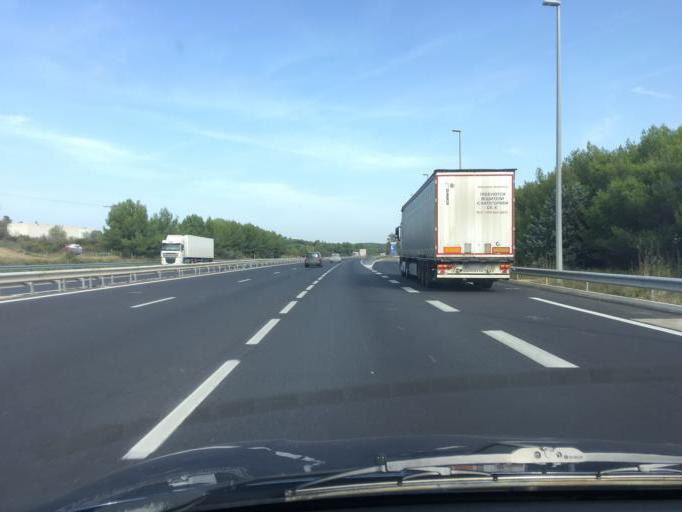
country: FR
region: Languedoc-Roussillon
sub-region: Departement du Gard
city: Marguerittes
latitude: 43.8661
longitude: 4.4351
